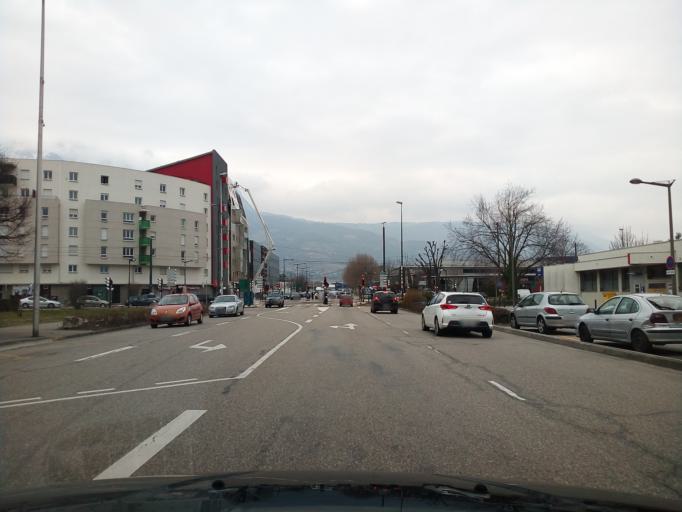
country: FR
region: Rhone-Alpes
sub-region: Departement de l'Isere
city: Echirolles
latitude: 45.1496
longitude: 5.7190
